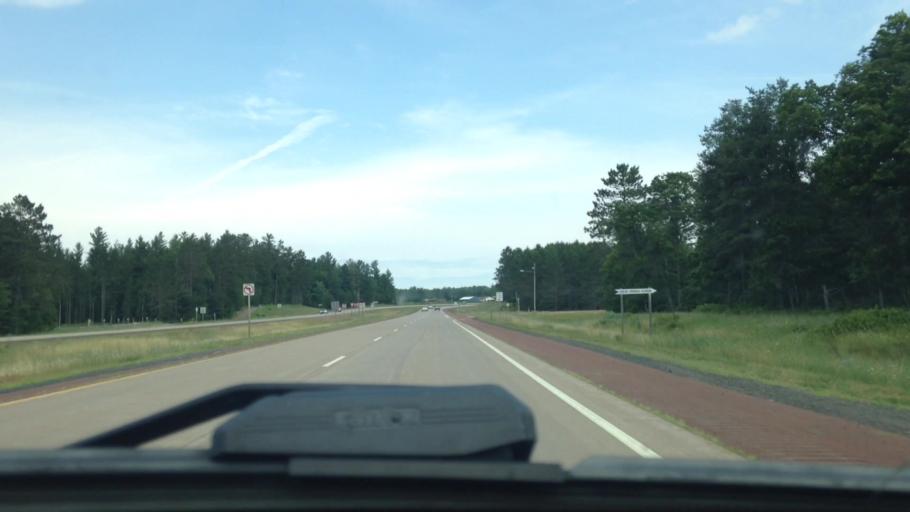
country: US
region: Wisconsin
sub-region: Douglas County
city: Lake Nebagamon
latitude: 46.3438
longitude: -91.8342
